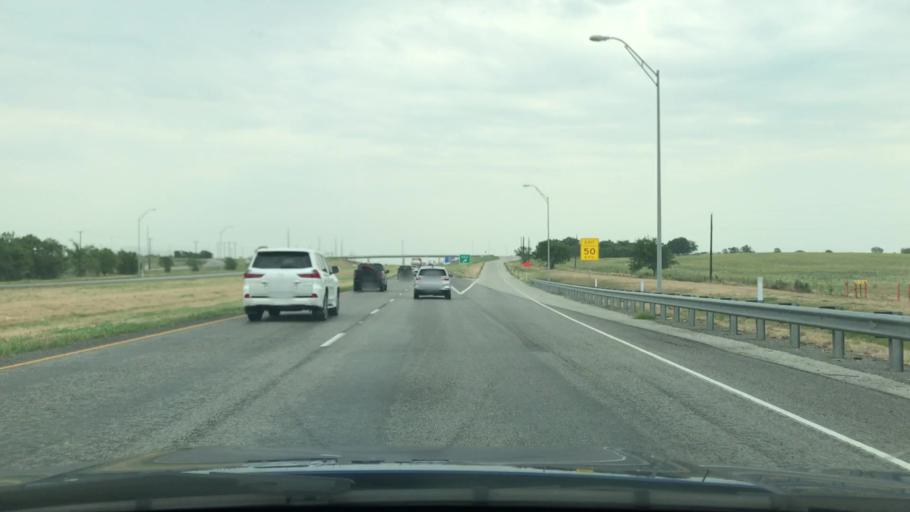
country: US
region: Texas
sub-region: Kaufman County
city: Talty
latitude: 32.7322
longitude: -96.3463
